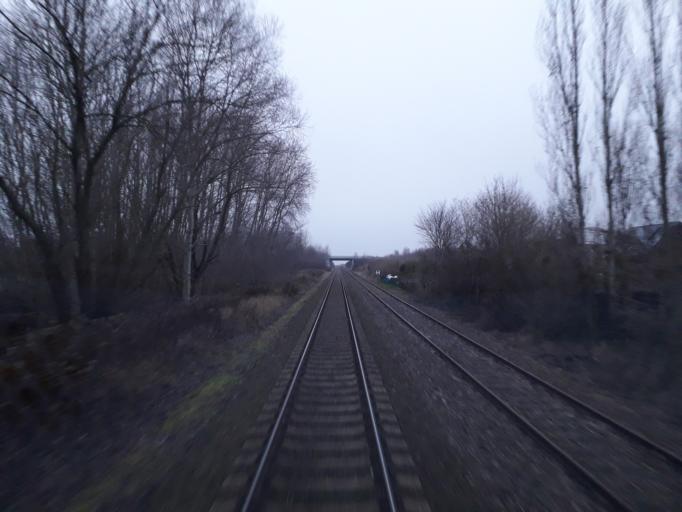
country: DE
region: Brandenburg
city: Pritzwalk
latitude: 53.1446
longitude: 12.1618
